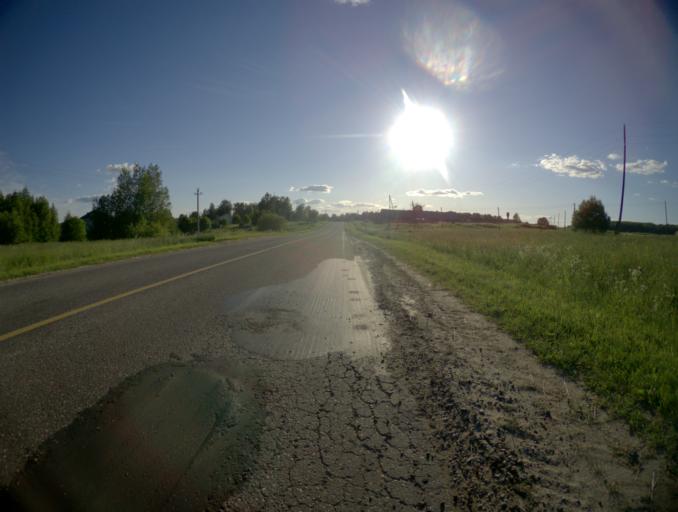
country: RU
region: Ivanovo
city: Lezhnevo
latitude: 56.8242
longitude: 40.8725
